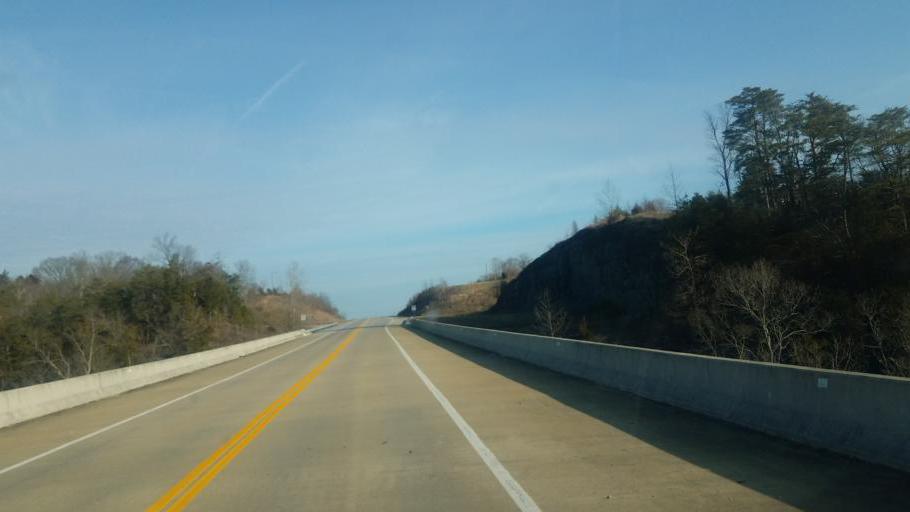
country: US
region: Kentucky
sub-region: Russell County
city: Jamestown
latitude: 36.9698
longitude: -85.0872
